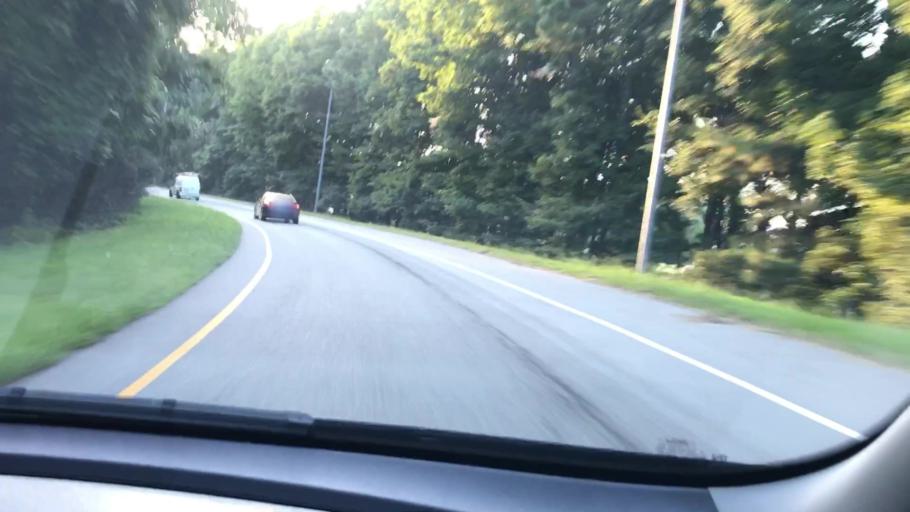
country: US
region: Virginia
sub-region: City of Hampton
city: Hampton
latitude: 37.0610
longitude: -76.4161
